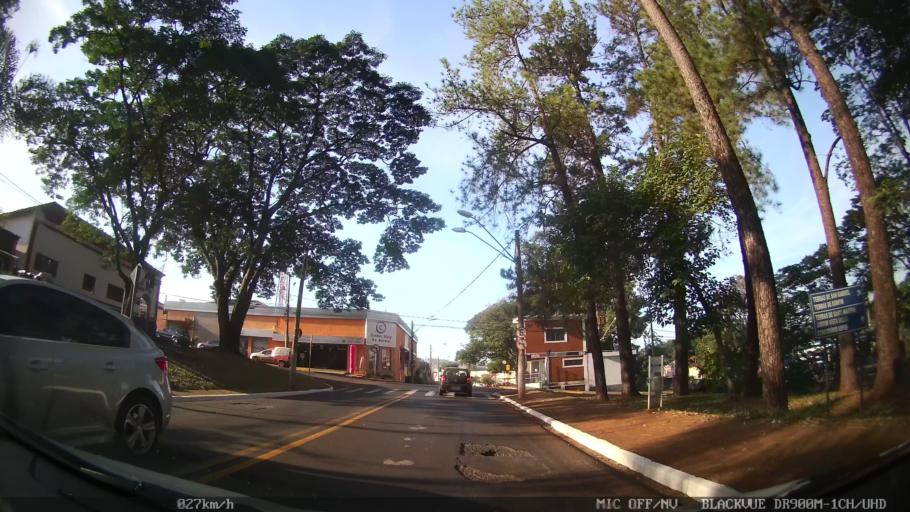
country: BR
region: Sao Paulo
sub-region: Ribeirao Preto
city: Ribeirao Preto
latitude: -21.2661
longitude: -47.8180
